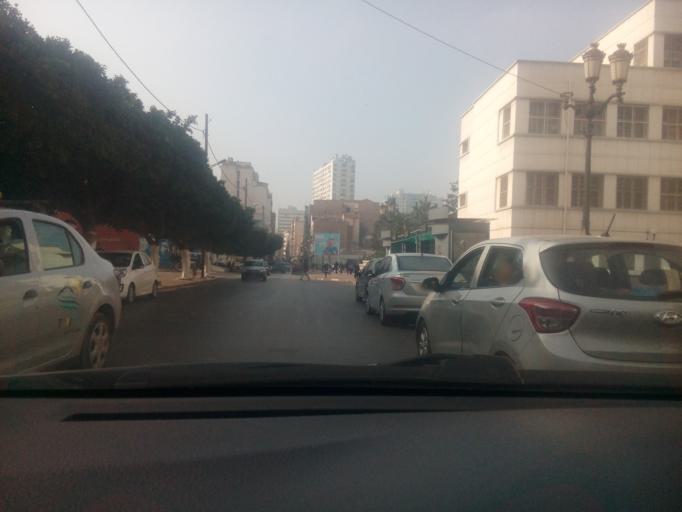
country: DZ
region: Oran
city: Oran
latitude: 35.7053
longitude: -0.6304
